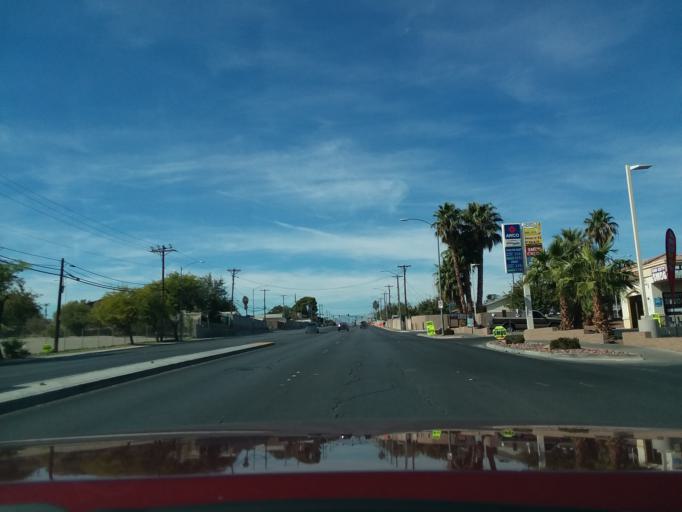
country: US
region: Nevada
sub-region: Clark County
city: Las Vegas
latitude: 36.1958
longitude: -115.1432
